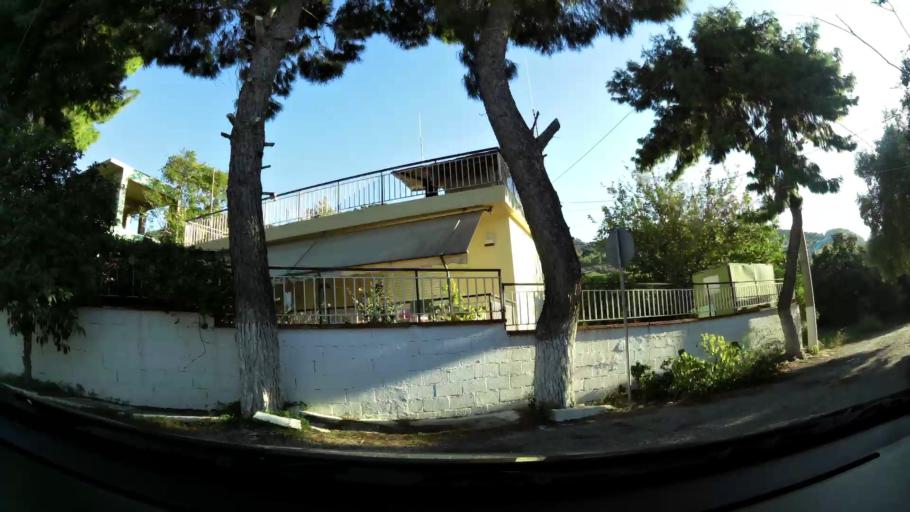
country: GR
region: Attica
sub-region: Nomarchia Athinas
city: Chaidari
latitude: 38.0345
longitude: 23.6342
